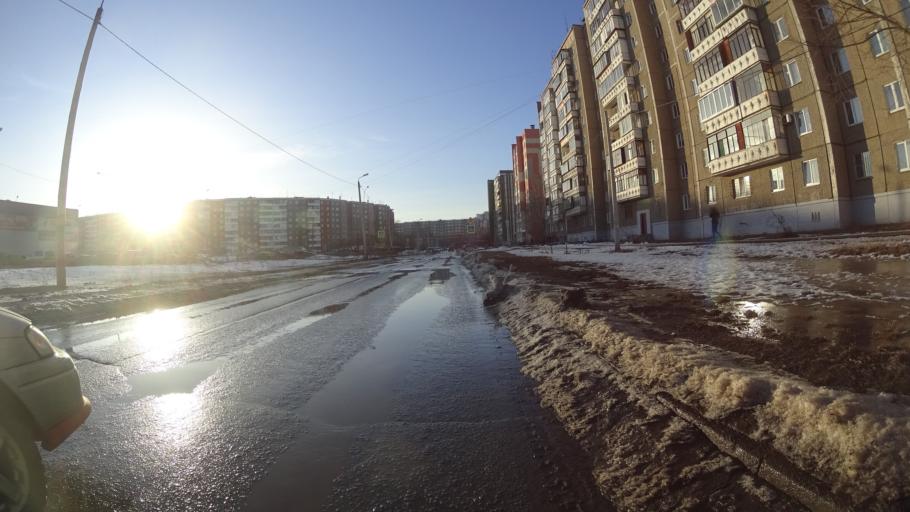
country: RU
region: Chelyabinsk
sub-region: Gorod Chelyabinsk
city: Chelyabinsk
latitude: 55.1359
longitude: 61.4535
